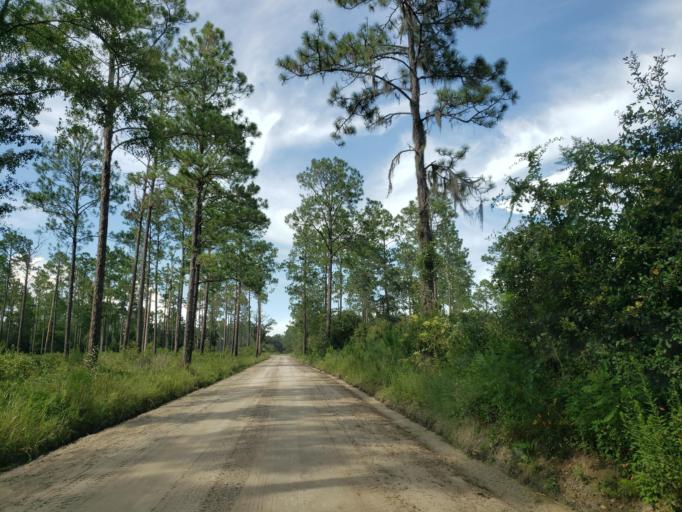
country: US
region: Georgia
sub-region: Echols County
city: Statenville
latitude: 30.6228
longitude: -83.2000
